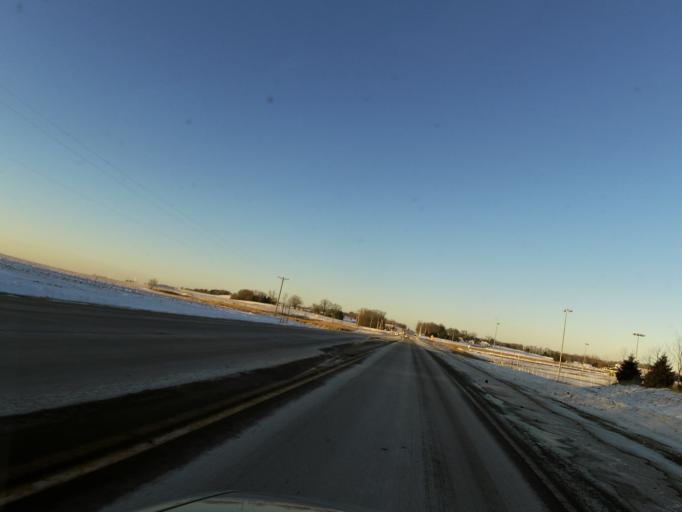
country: US
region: Minnesota
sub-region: Dakota County
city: Farmington
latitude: 44.6695
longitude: -93.1366
